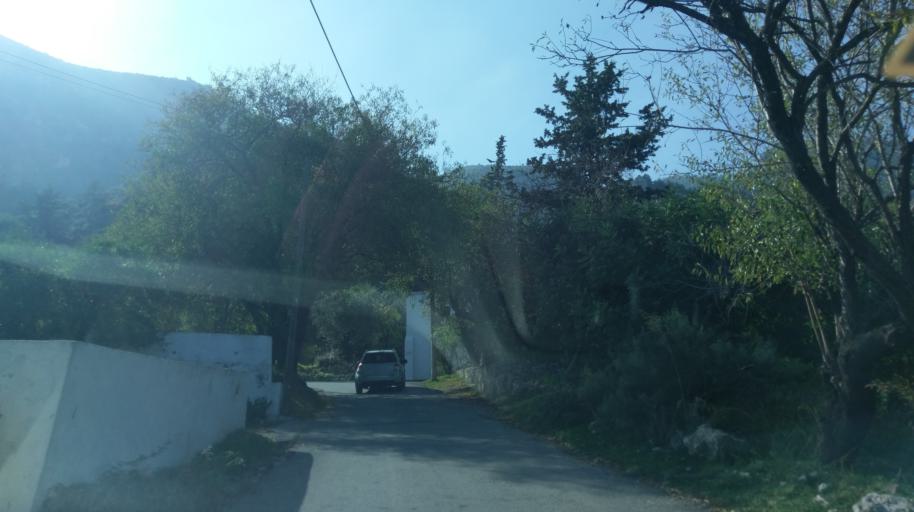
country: CY
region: Keryneia
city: Kyrenia
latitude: 35.3181
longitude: 33.2589
